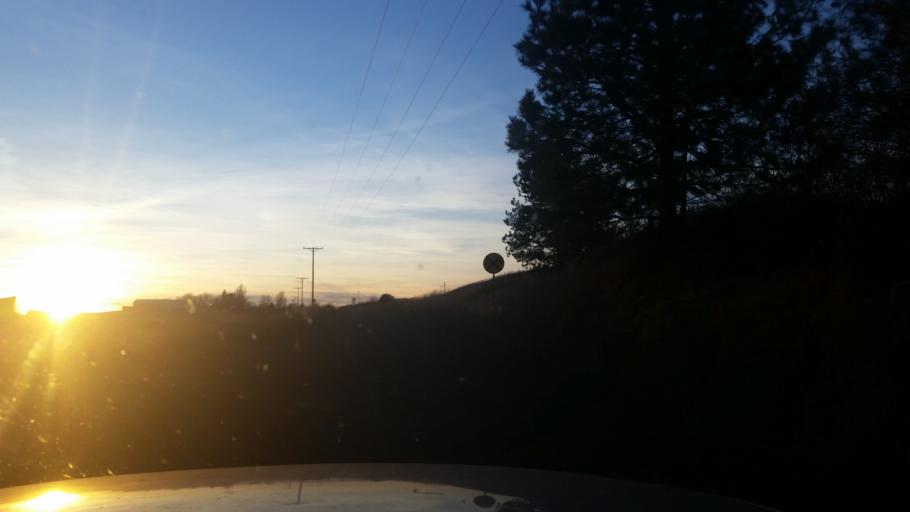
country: US
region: Washington
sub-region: Spokane County
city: Veradale
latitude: 47.5077
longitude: -117.1241
